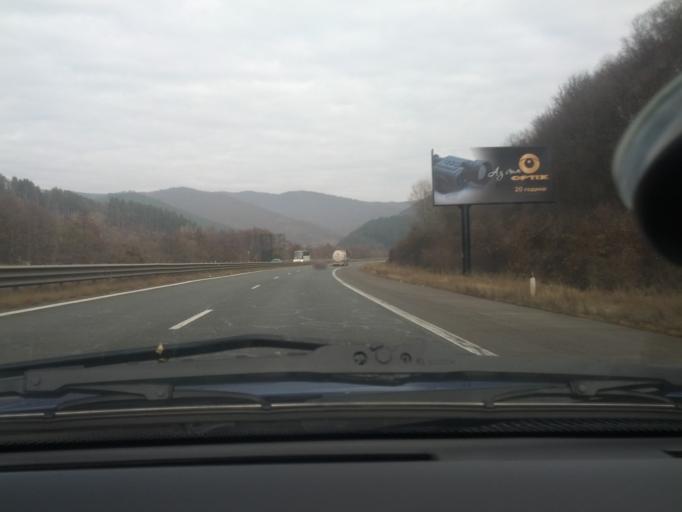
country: BG
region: Sofiya
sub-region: Obshtina Gorna Malina
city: Gorna Malina
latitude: 42.7663
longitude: 23.7109
